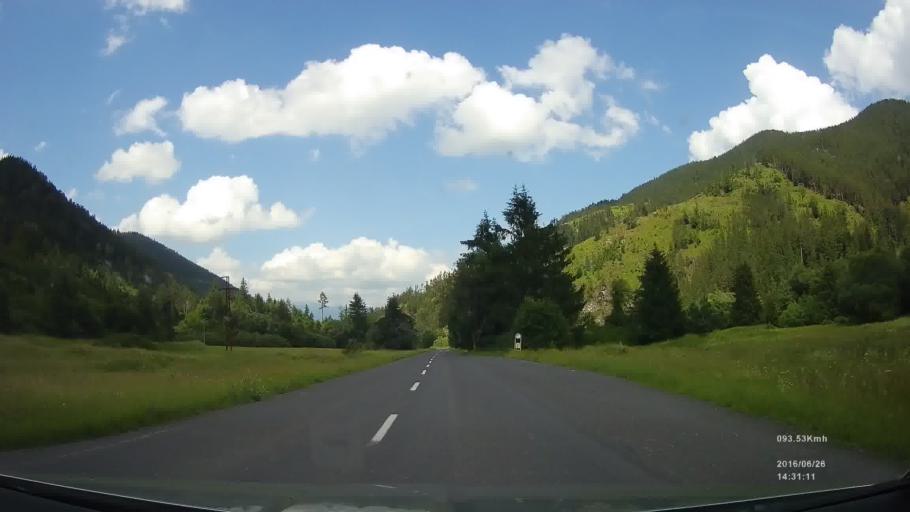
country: SK
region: Zilinsky
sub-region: Okres Zilina
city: Liptovsky Hradok
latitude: 48.9987
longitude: 19.7638
